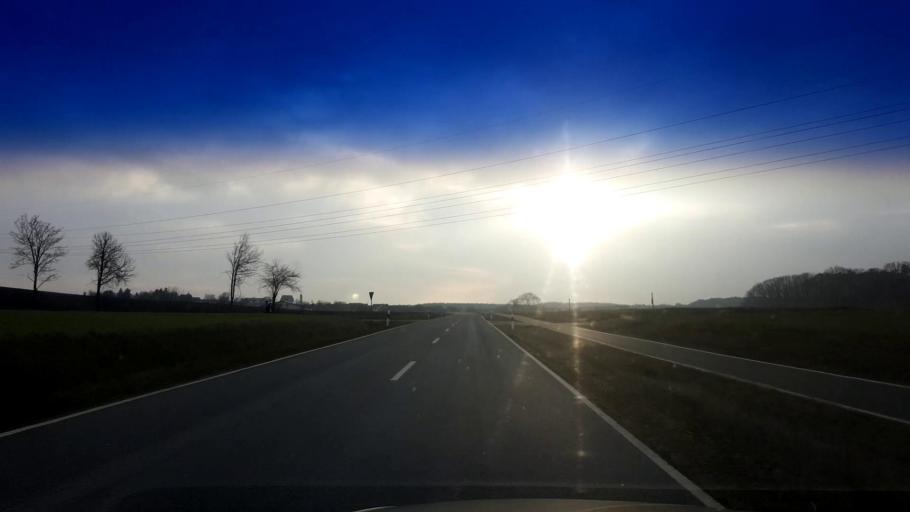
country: DE
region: Bavaria
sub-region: Upper Franconia
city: Hallerndorf
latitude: 49.7917
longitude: 10.9621
